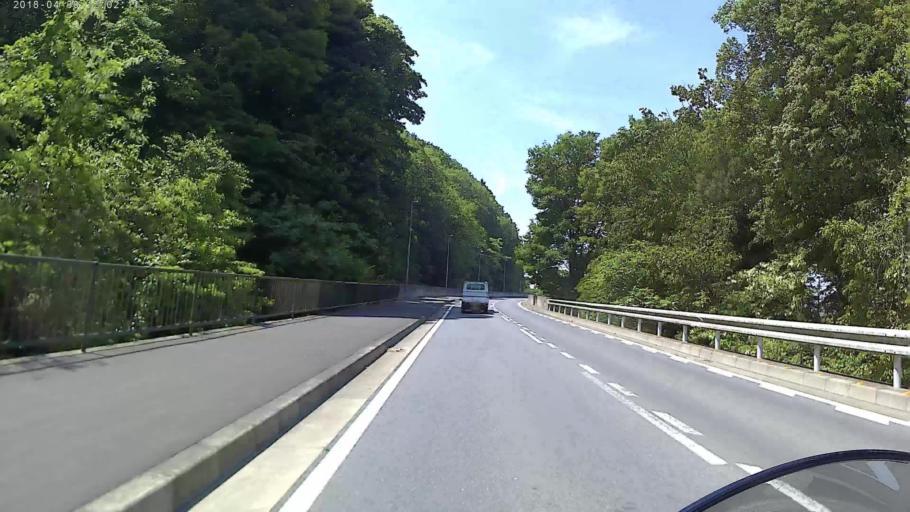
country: JP
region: Kanagawa
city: Zama
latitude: 35.5211
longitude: 139.3201
